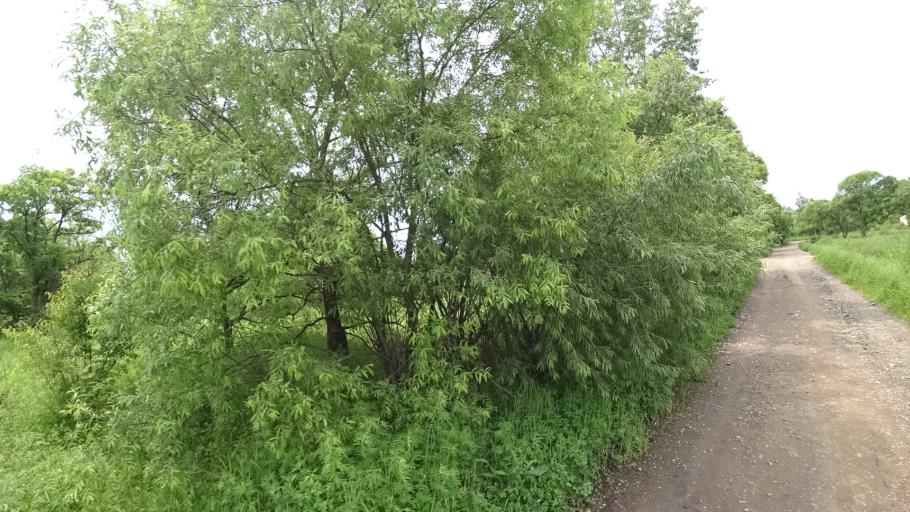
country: RU
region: Primorskiy
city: Novosysoyevka
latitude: 44.2263
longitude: 133.3634
